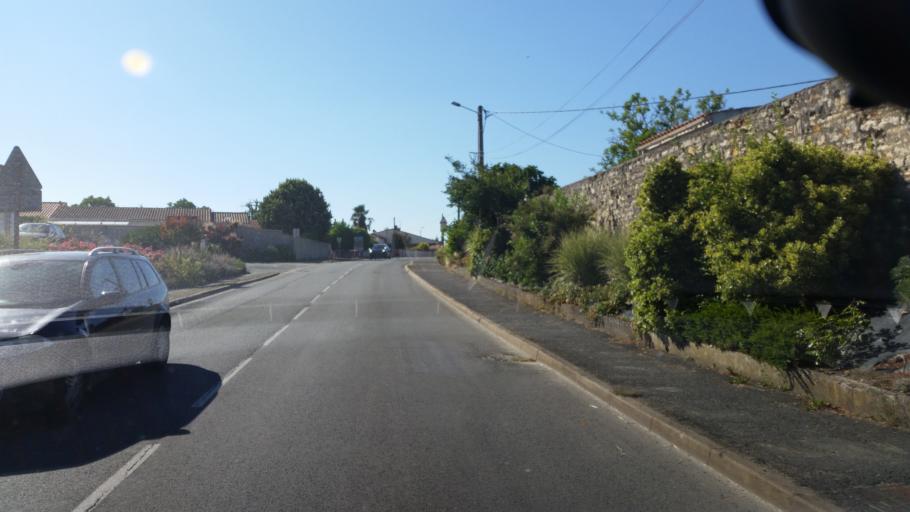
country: FR
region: Poitou-Charentes
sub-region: Departement de la Charente-Maritime
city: Marans
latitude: 46.3037
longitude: -0.9860
